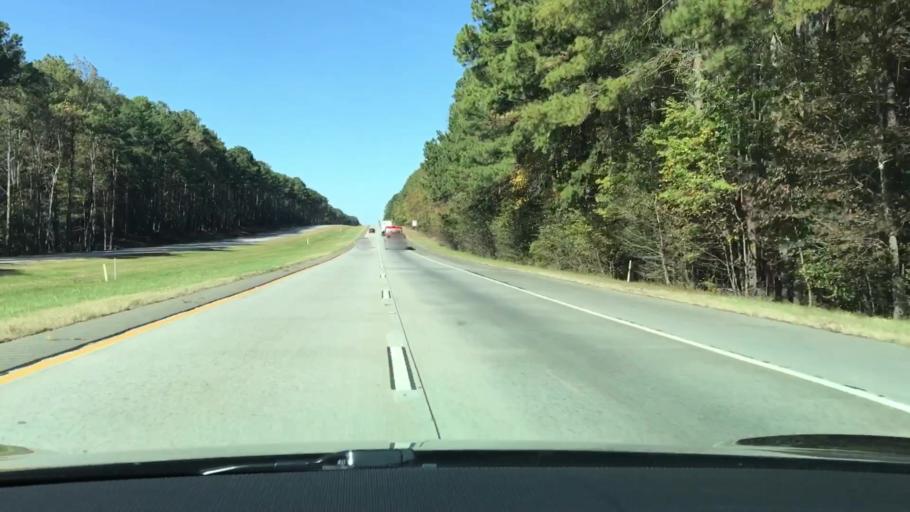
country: US
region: Georgia
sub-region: Taliaferro County
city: Crawfordville
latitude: 33.5039
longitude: -82.8286
